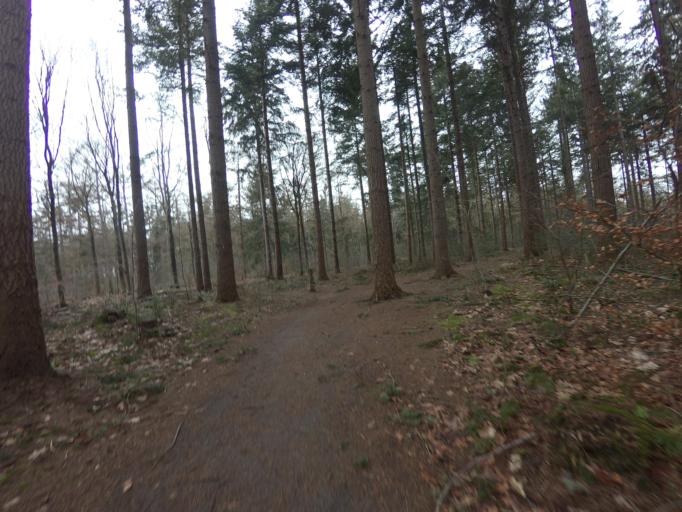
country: NL
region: Friesland
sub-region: Gemeente Gaasterlan-Sleat
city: Oudemirdum
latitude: 52.8614
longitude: 5.5419
